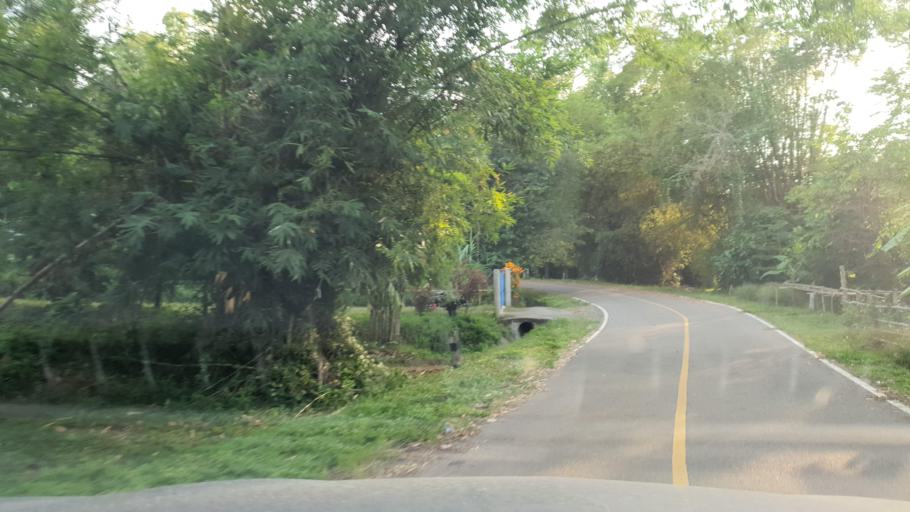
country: TH
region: Chiang Mai
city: Mae On
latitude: 18.8674
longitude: 99.2415
